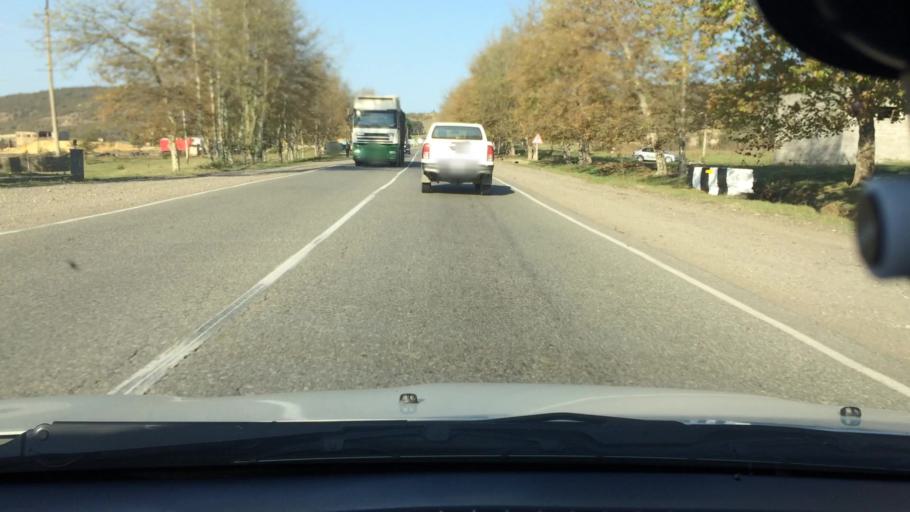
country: GE
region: Imereti
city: Kutaisi
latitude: 42.2144
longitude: 42.8157
